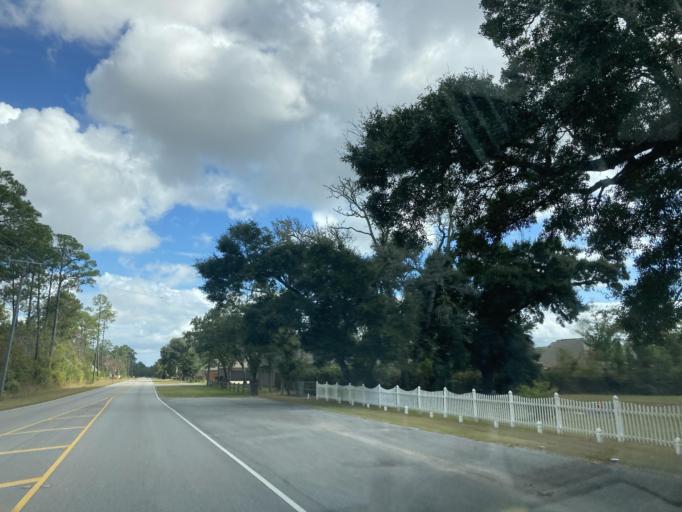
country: US
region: Mississippi
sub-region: Jackson County
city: Gulf Hills
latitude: 30.4518
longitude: -88.8261
